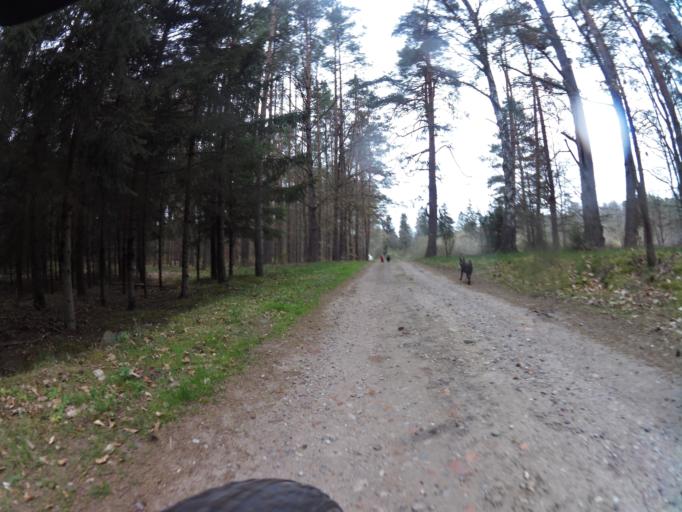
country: PL
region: West Pomeranian Voivodeship
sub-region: Powiat koszalinski
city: Polanow
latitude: 54.0471
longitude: 16.6209
